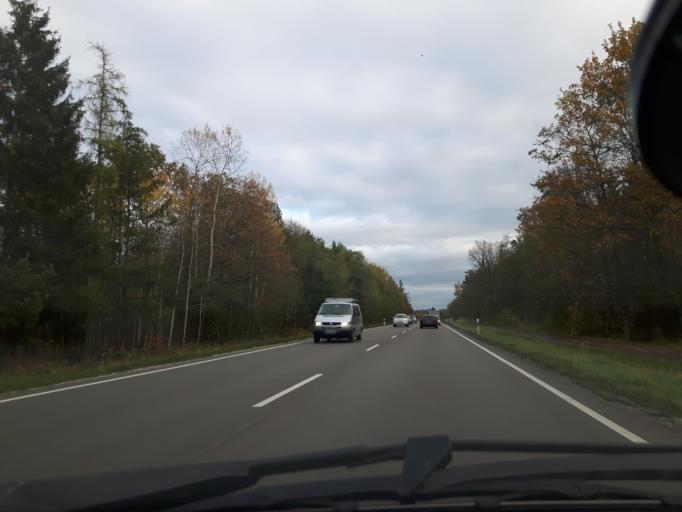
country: DE
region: Bavaria
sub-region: Regierungsbezirk Mittelfranken
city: Burgoberbach
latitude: 49.2375
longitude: 10.6118
